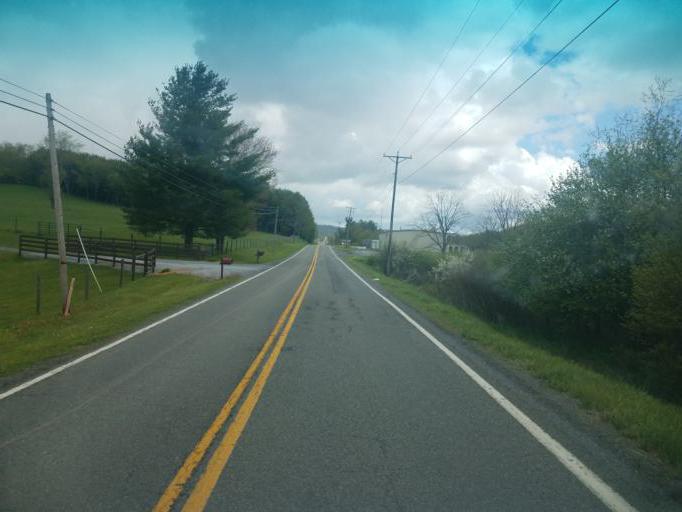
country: US
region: Virginia
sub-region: Bland County
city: Bland
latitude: 37.0885
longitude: -81.1411
